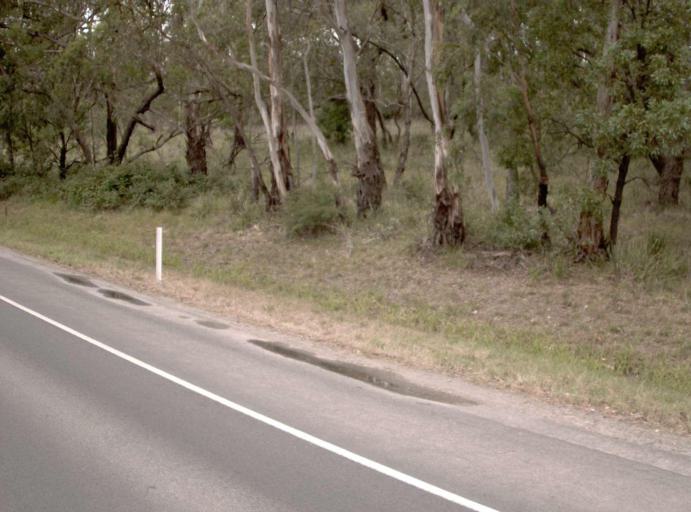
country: AU
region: Victoria
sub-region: Yarra Ranges
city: Lilydale
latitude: -37.7416
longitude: 145.3733
